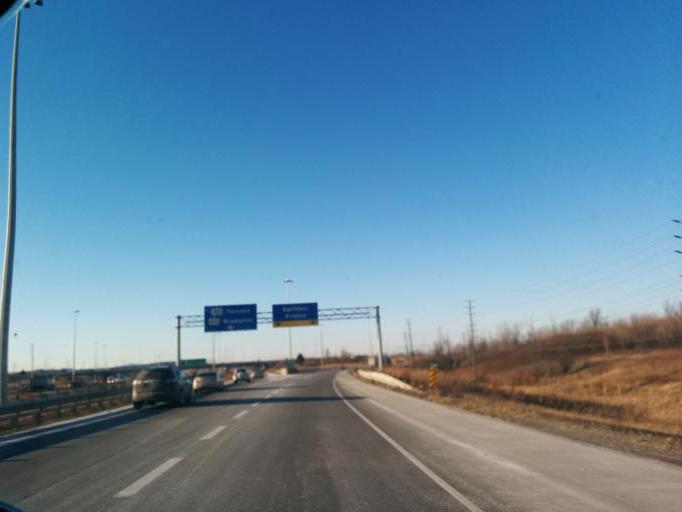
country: CA
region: Ontario
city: Mississauga
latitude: 43.6188
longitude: -79.6321
